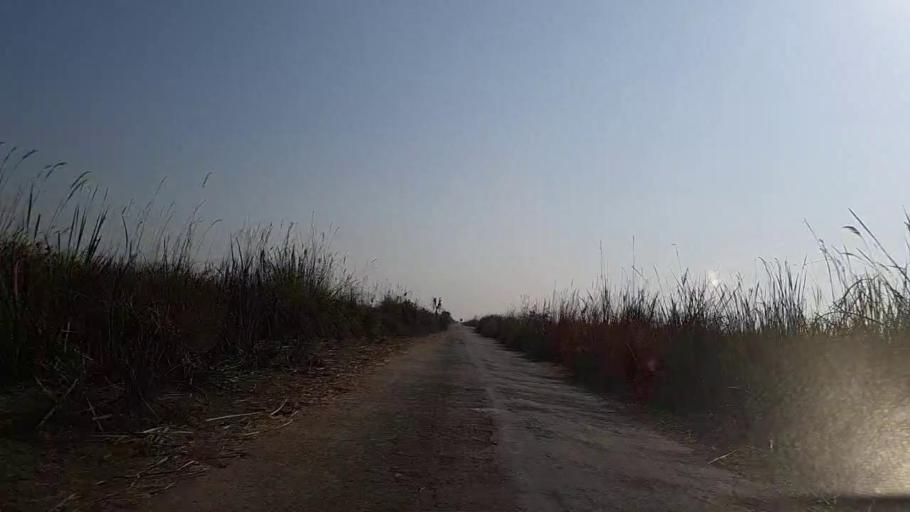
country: PK
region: Sindh
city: Tando Mittha Khan
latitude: 25.8931
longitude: 69.0769
